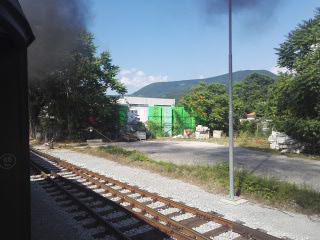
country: SI
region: Nova Gorica
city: Solkan
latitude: 45.9648
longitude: 13.6390
